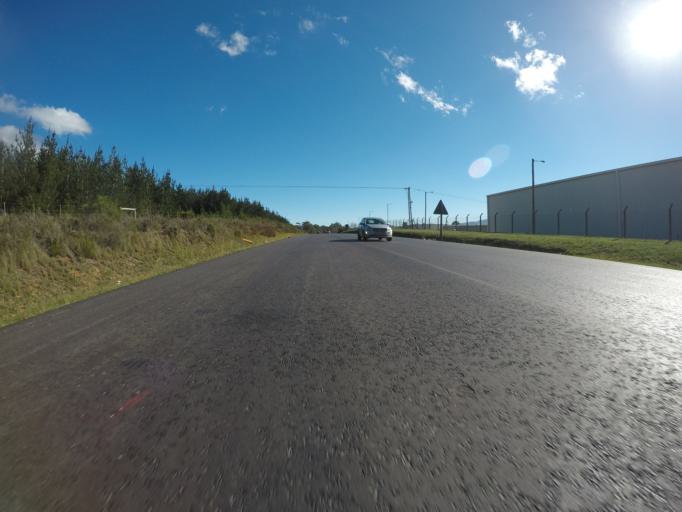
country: ZA
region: Western Cape
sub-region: Overberg District Municipality
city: Grabouw
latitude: -34.1782
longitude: 19.0709
